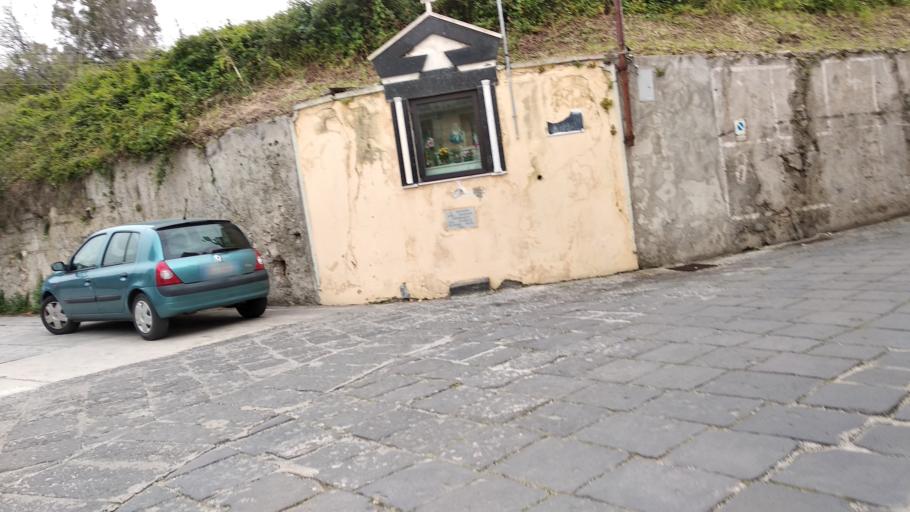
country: IT
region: Sicily
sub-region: Messina
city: Saponara Marittima
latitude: 38.2342
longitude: 15.4301
